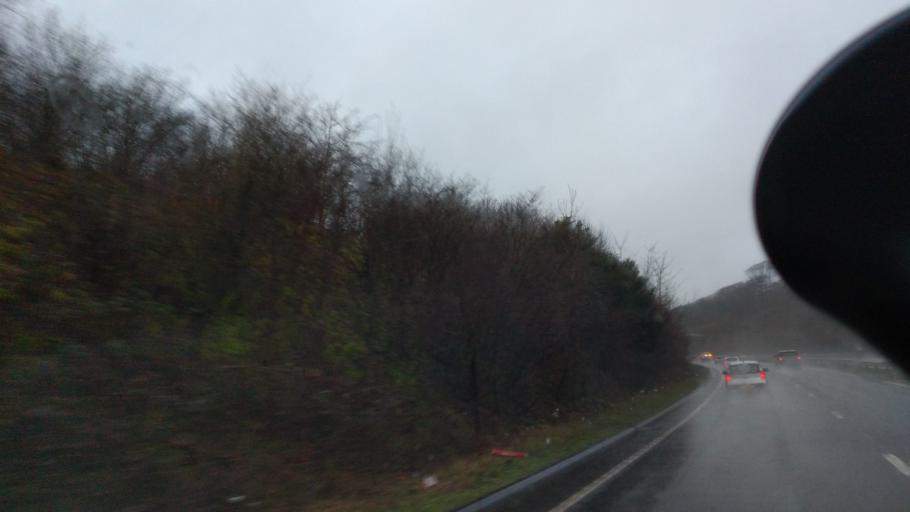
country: GB
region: England
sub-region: Brighton and Hove
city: Brighton
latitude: 50.8637
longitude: -0.1057
